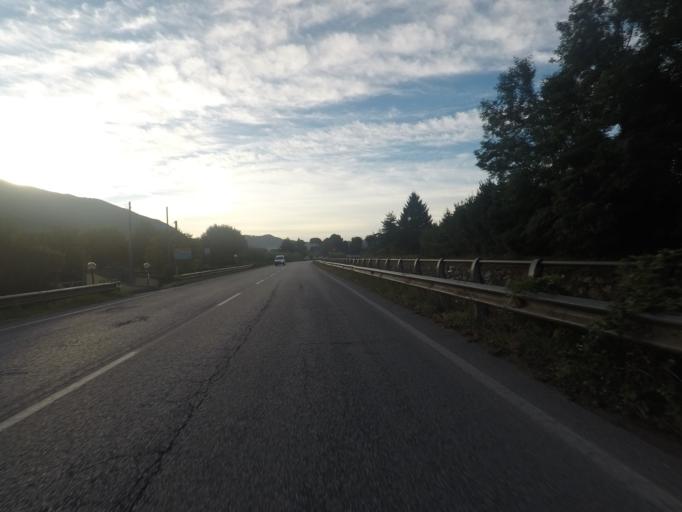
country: IT
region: Tuscany
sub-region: Provincia di Lucca
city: Corsanico-Bargecchia
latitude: 43.9356
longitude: 10.3045
